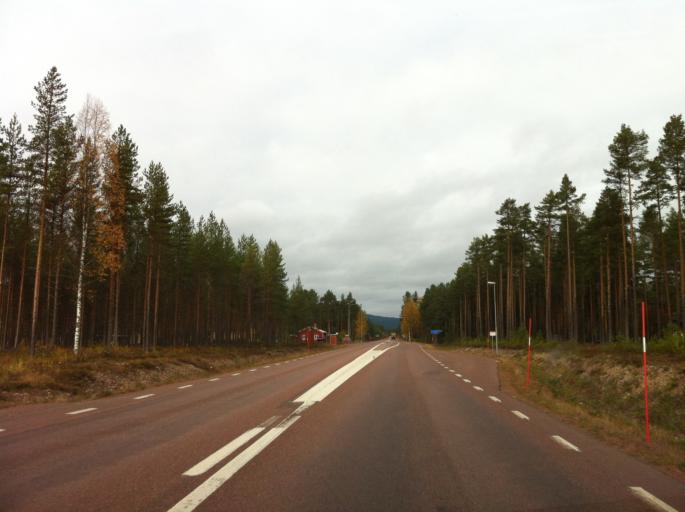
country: SE
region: Dalarna
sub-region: Alvdalens Kommun
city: AElvdalen
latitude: 61.2557
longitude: 14.0308
